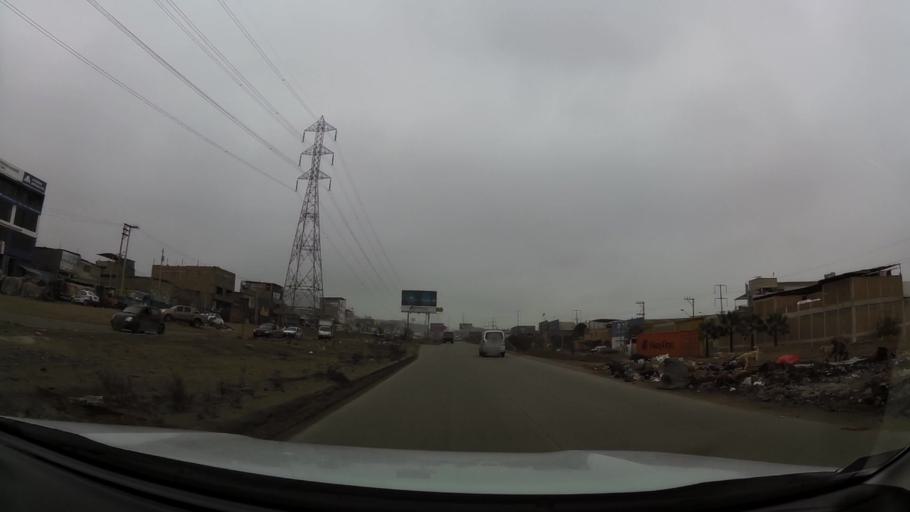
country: PE
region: Lima
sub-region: Lima
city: Surco
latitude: -12.1989
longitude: -76.9328
